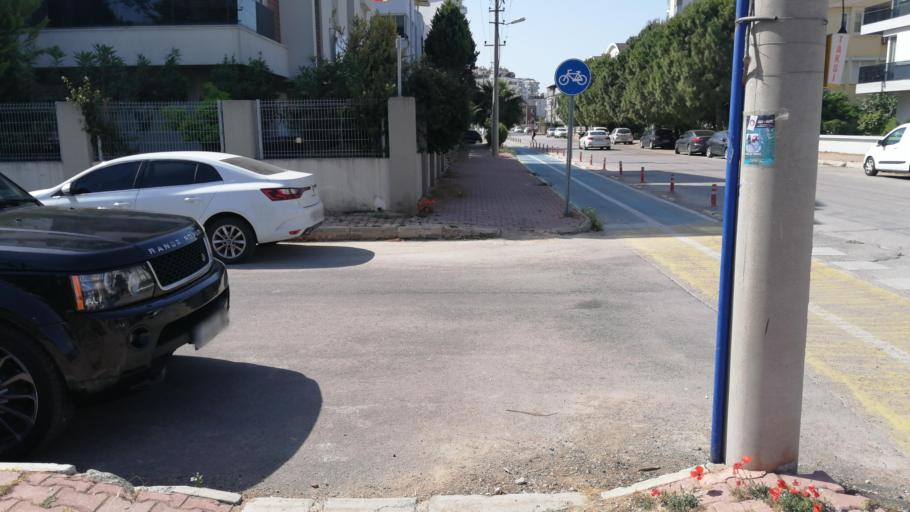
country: TR
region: Antalya
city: Antalya
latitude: 36.8587
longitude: 30.7832
